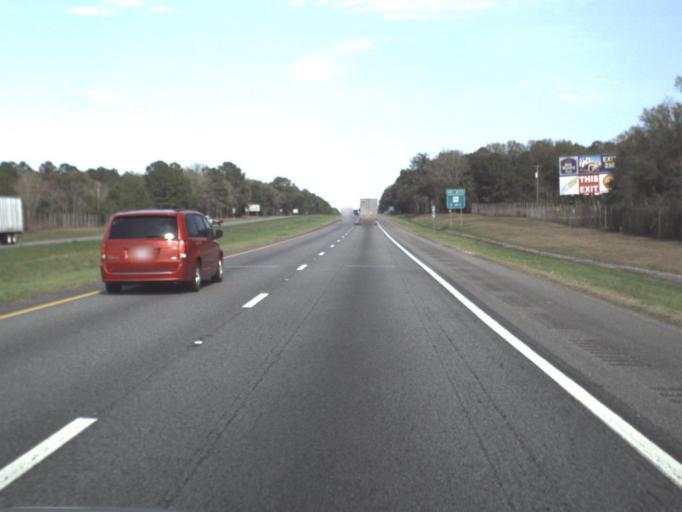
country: US
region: Florida
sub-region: Jefferson County
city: Monticello
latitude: 30.4822
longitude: -84.0474
